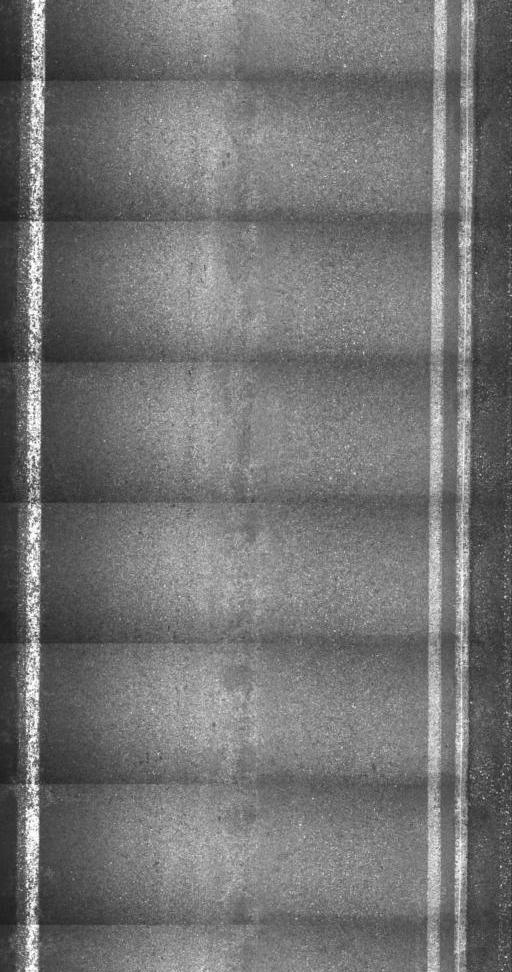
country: CA
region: Quebec
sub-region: Monteregie
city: Sutton
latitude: 44.9880
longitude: -72.4968
